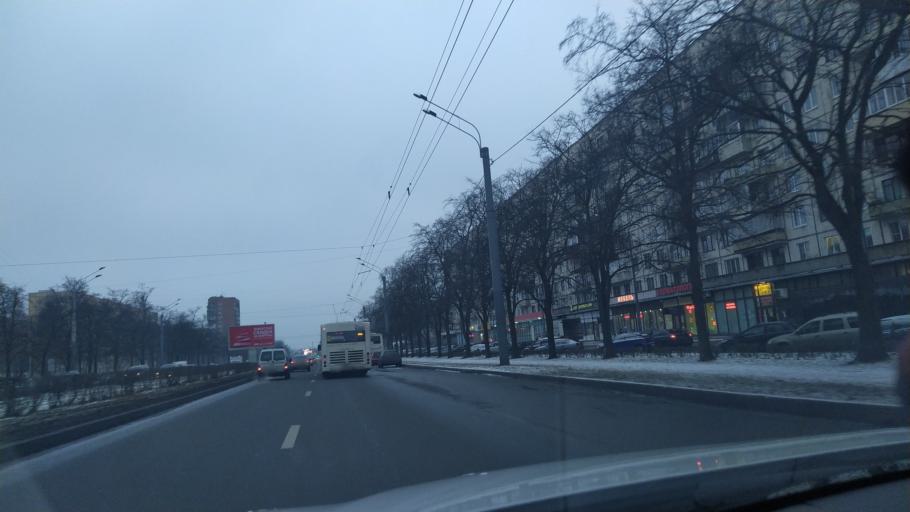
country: RU
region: St.-Petersburg
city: Grazhdanka
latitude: 60.0373
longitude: 30.3966
